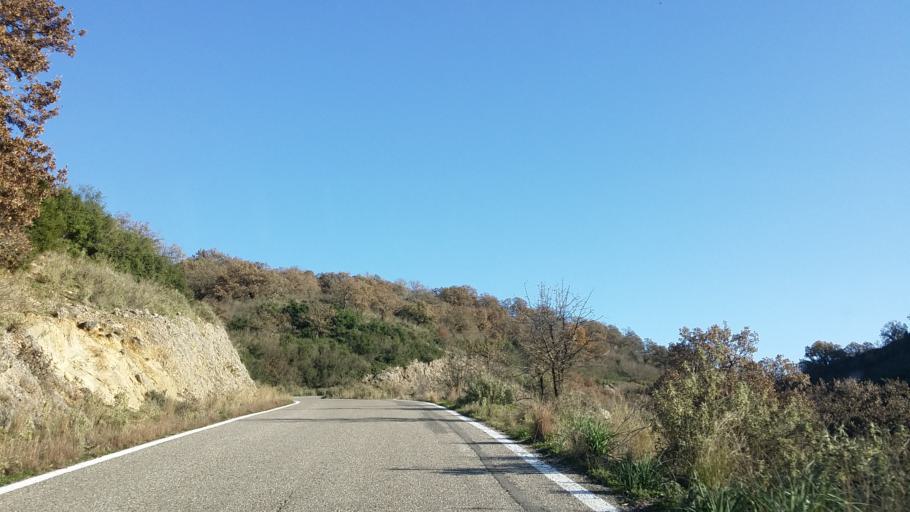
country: GR
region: West Greece
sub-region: Nomos Aitolias kai Akarnanias
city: Fitiai
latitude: 38.6385
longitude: 21.1895
